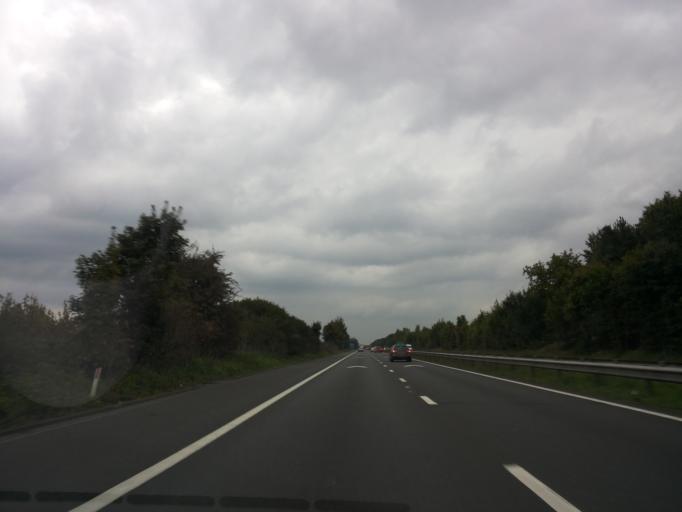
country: GB
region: England
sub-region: Kent
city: Teynham
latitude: 51.2967
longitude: 0.7947
